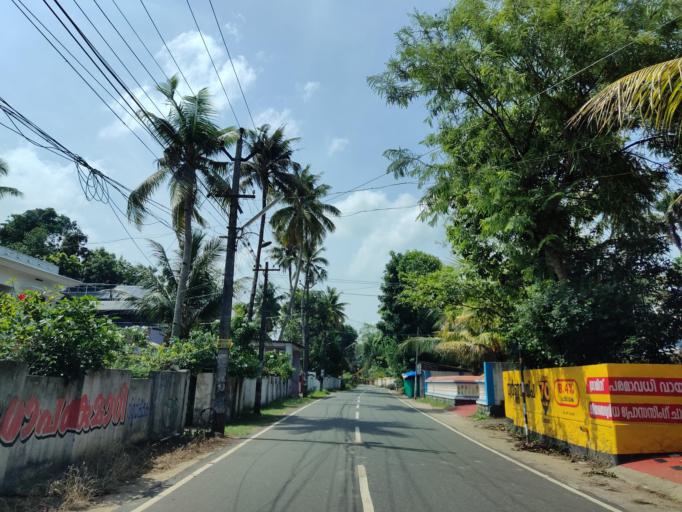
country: IN
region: Kerala
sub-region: Alappuzha
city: Mavelikara
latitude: 9.3193
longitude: 76.5282
